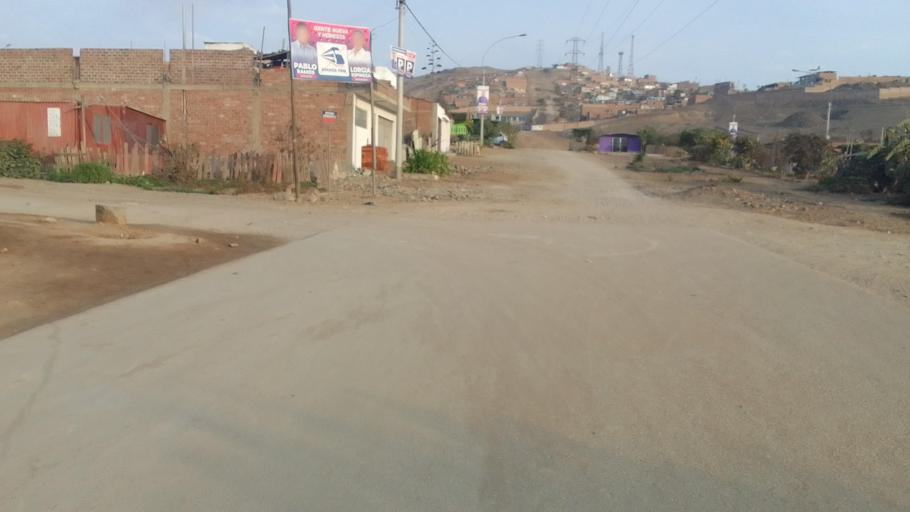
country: PE
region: Lima
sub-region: Lima
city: Santa Rosa
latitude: -11.8180
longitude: -77.1223
